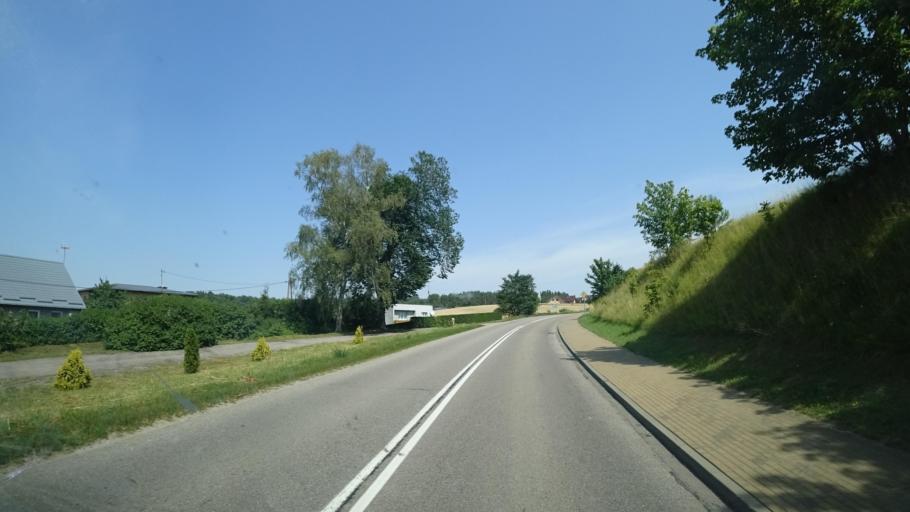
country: PL
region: Pomeranian Voivodeship
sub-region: Powiat koscierski
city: Dziemiany
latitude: 53.9722
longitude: 17.7648
